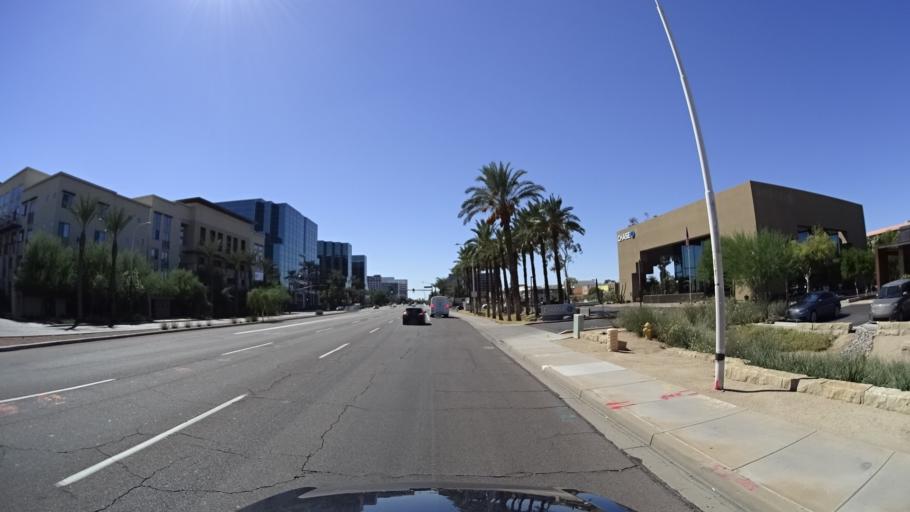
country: US
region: Arizona
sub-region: Maricopa County
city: Phoenix
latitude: 33.5097
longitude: -112.0242
